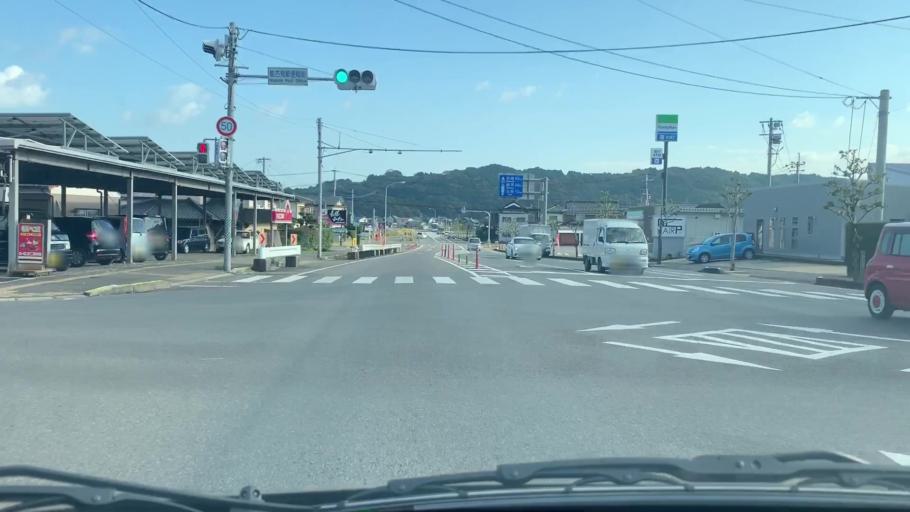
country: JP
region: Saga Prefecture
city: Kashima
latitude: 33.0944
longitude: 130.0937
